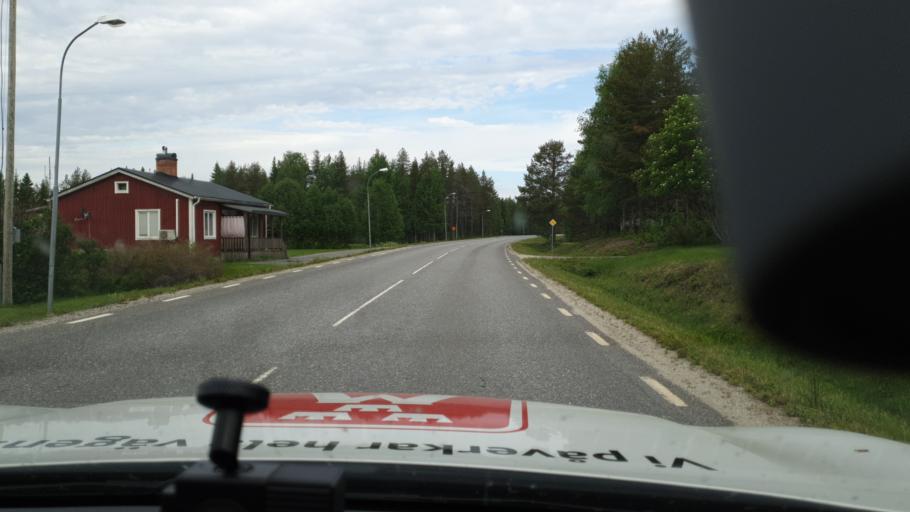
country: SE
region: Vaesterbotten
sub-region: Mala Kommun
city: Mala
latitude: 64.9903
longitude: 18.4960
